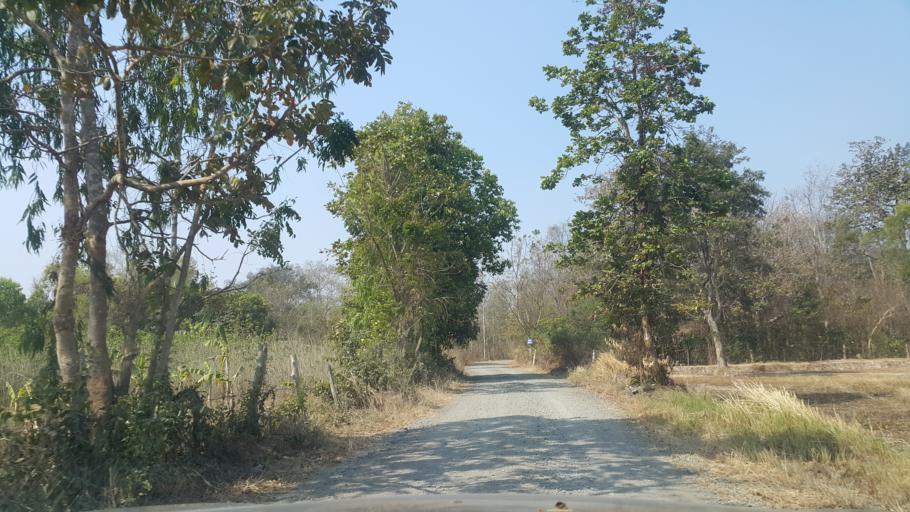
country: TH
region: Buriram
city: Krasang
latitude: 15.0922
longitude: 103.3737
